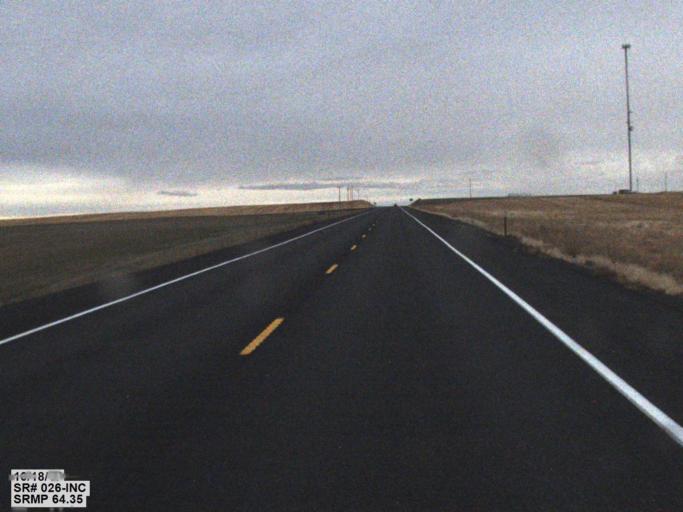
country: US
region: Washington
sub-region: Franklin County
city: Connell
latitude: 46.7944
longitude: -118.6789
